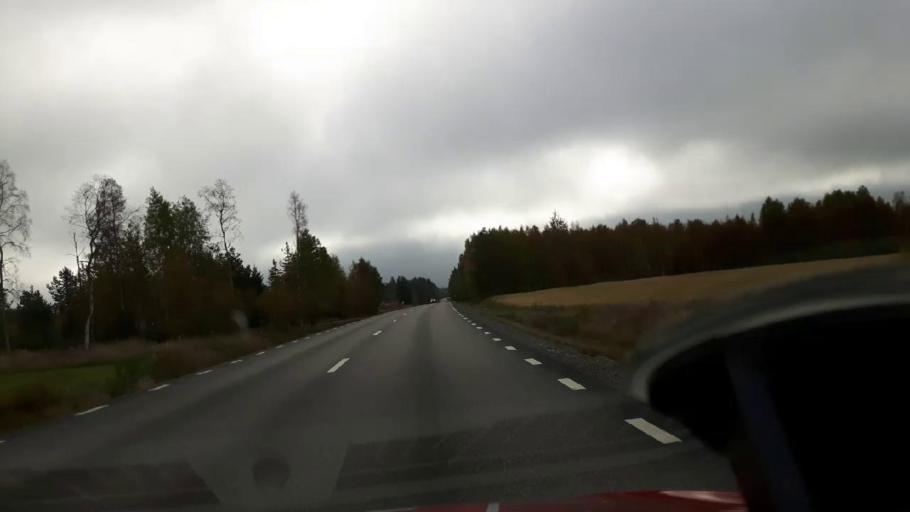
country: SE
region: Gaevleborg
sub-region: Ljusdals Kommun
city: Farila
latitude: 61.8619
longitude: 15.7406
